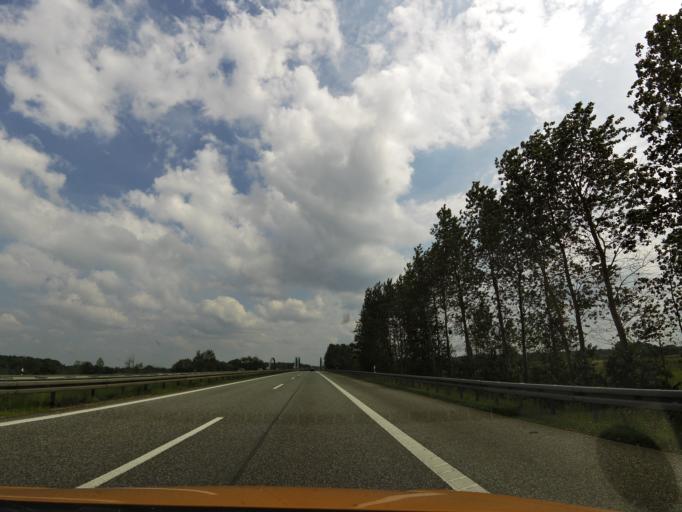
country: DE
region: Mecklenburg-Vorpommern
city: Neustadt-Glewe
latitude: 53.3951
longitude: 11.5910
